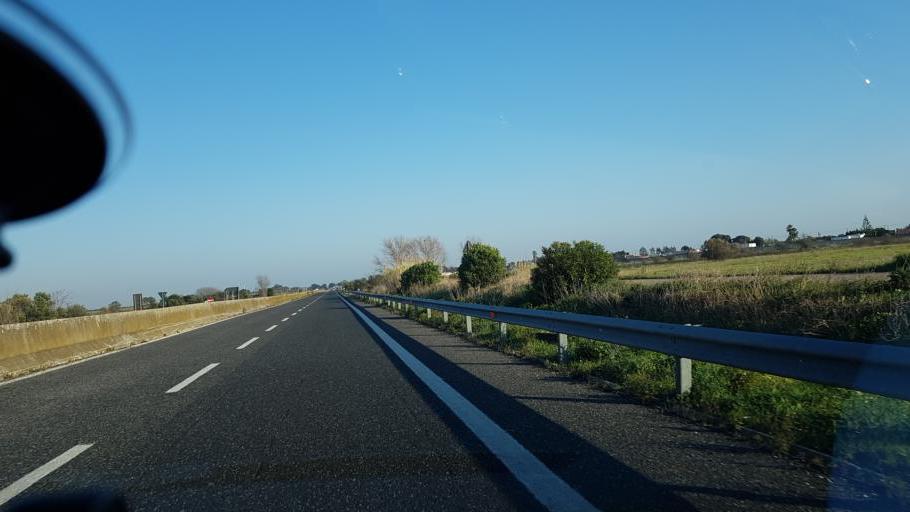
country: IT
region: Apulia
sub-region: Provincia di Brindisi
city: Brindisi
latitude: 40.6773
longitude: 17.8450
